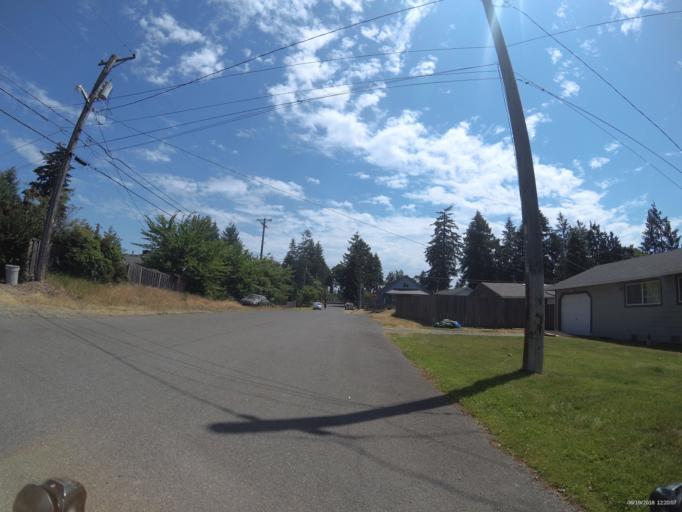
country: US
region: Washington
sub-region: Pierce County
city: Lakewood
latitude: 47.1752
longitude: -122.5327
